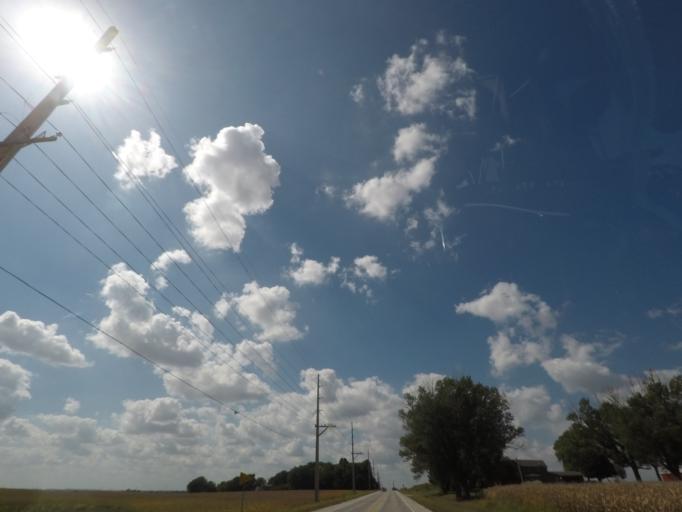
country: US
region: Iowa
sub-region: Story County
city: Ames
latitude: 42.0232
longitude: -93.5455
